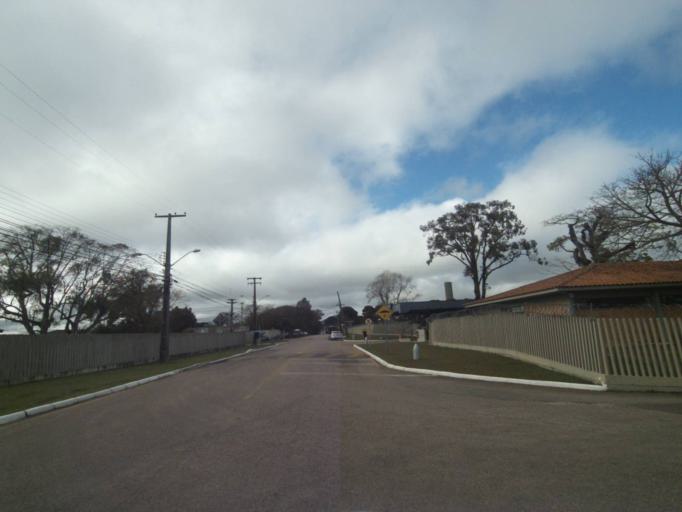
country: BR
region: Parana
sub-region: Sao Jose Dos Pinhais
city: Sao Jose dos Pinhais
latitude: -25.5287
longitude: -49.3016
